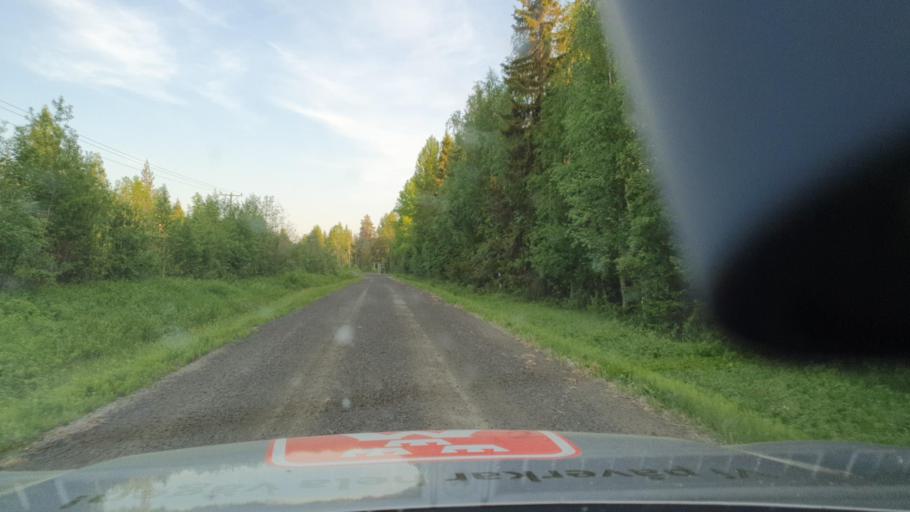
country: SE
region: Norrbotten
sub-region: Bodens Kommun
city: Boden
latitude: 66.1173
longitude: 21.5582
